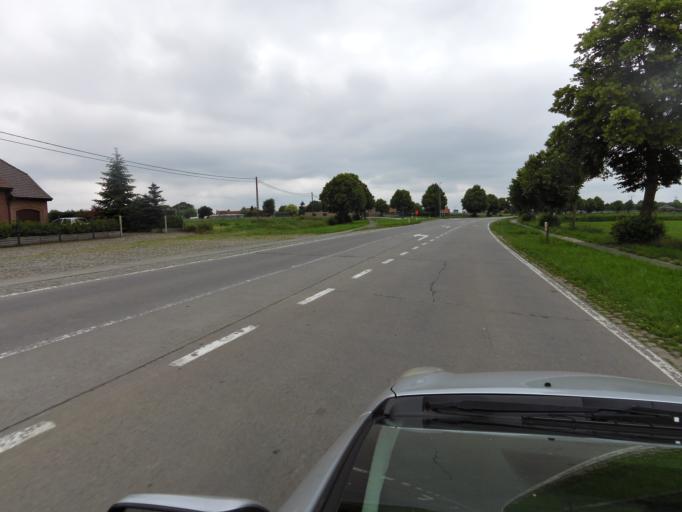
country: BE
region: Flanders
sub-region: Provincie West-Vlaanderen
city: Ieper
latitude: 50.9134
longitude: 2.8396
